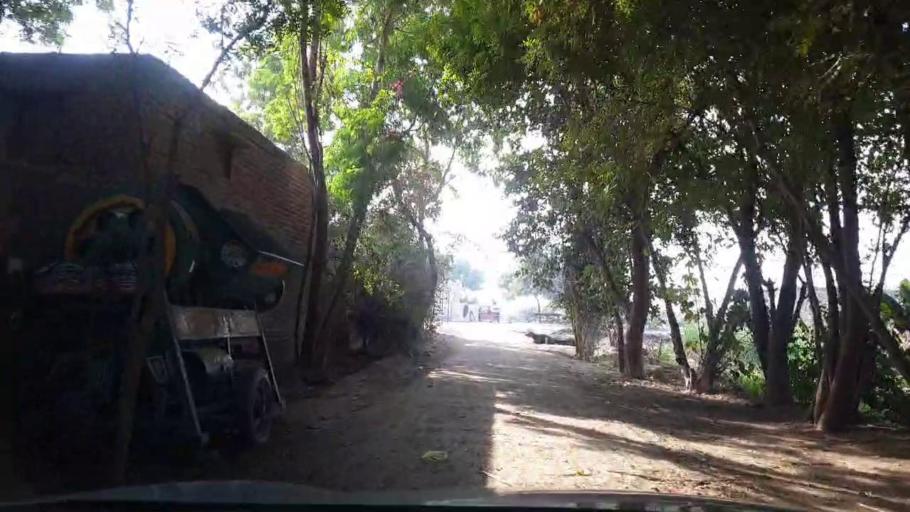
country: PK
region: Sindh
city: Tando Jam
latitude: 25.4669
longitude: 68.6195
